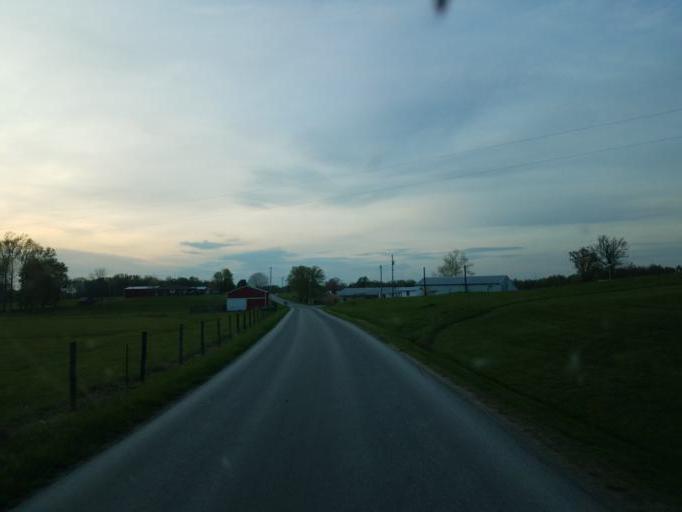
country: US
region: Kentucky
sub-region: Green County
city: Greensburg
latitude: 37.1811
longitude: -85.6850
